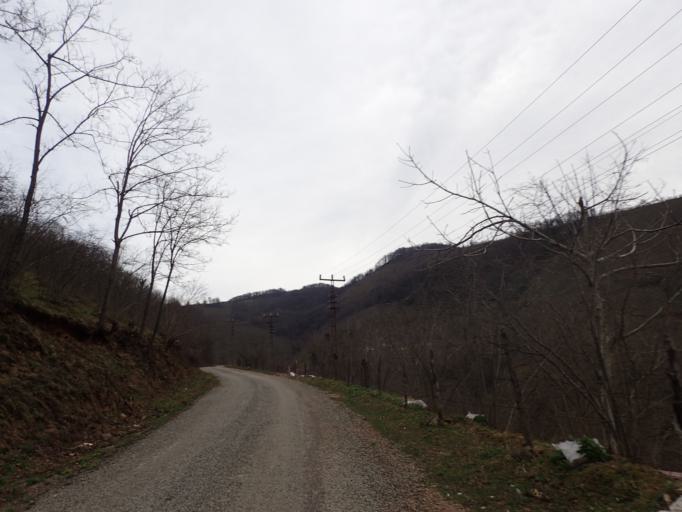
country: TR
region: Ordu
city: Camas
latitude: 40.8845
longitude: 37.5158
